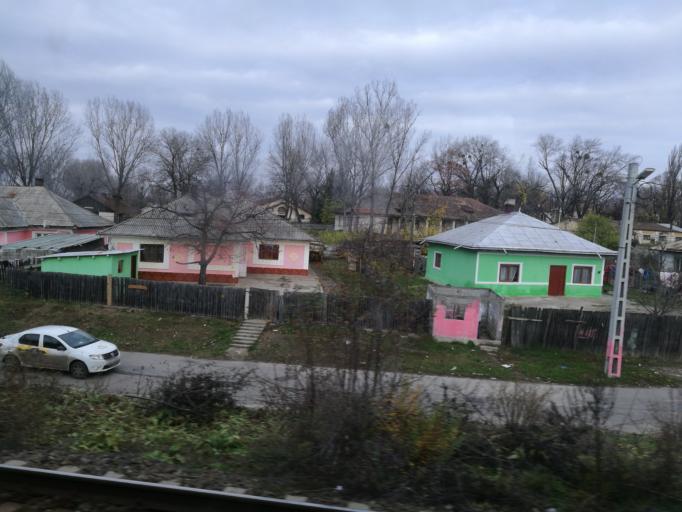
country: RO
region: Neamt
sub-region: Municipiul Roman
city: Roman
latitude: 46.9298
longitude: 26.9152
